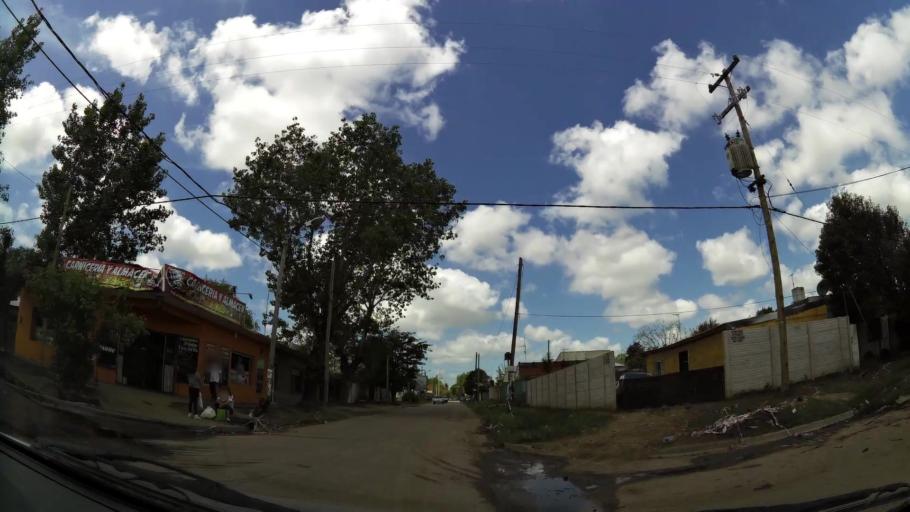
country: AR
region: Buenos Aires
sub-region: Partido de Quilmes
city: Quilmes
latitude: -34.8215
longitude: -58.2349
